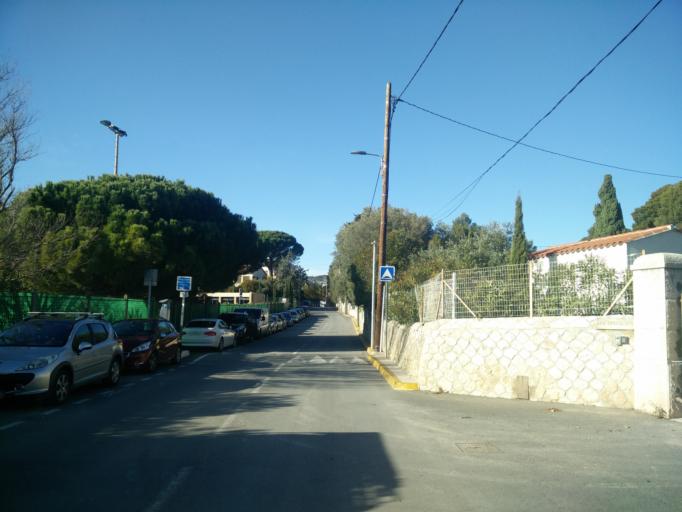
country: FR
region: Provence-Alpes-Cote d'Azur
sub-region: Departement des Bouches-du-Rhone
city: Cassis
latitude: 43.2120
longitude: 5.5442
